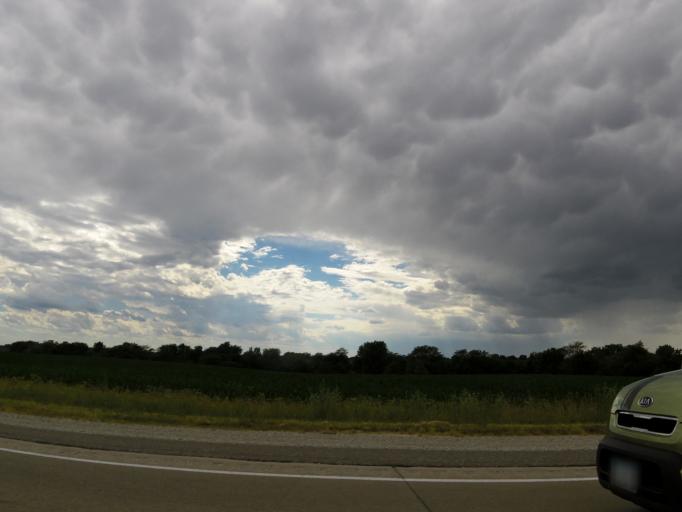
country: US
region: Iowa
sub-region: Henry County
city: Mount Pleasant
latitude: 41.0504
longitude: -91.5448
